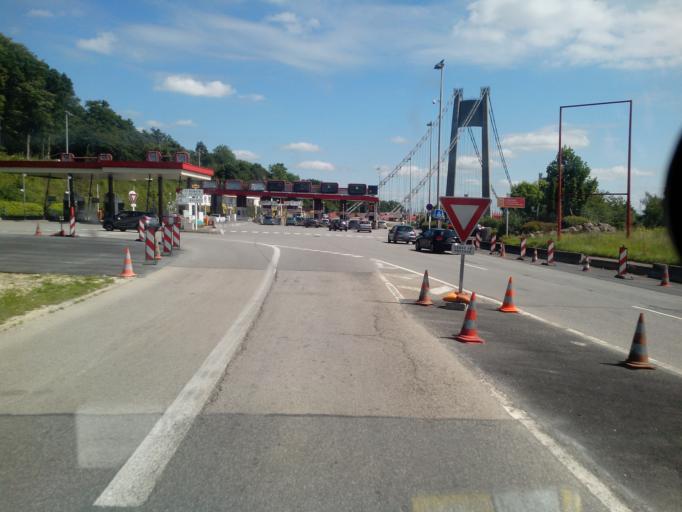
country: FR
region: Haute-Normandie
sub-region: Departement de la Seine-Maritime
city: Tancarville
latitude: 49.4775
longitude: 0.4586
